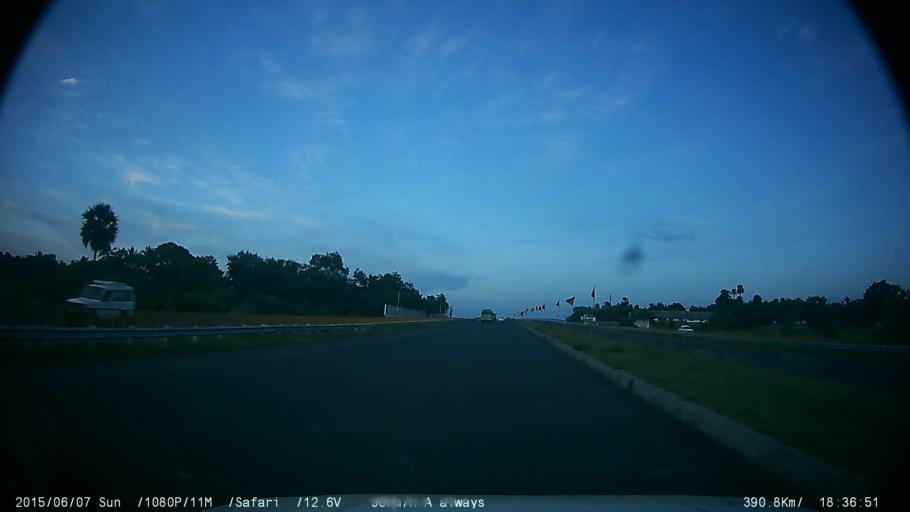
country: IN
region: Tamil Nadu
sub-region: Tiruppur
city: Avinashi
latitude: 11.1989
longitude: 77.3087
